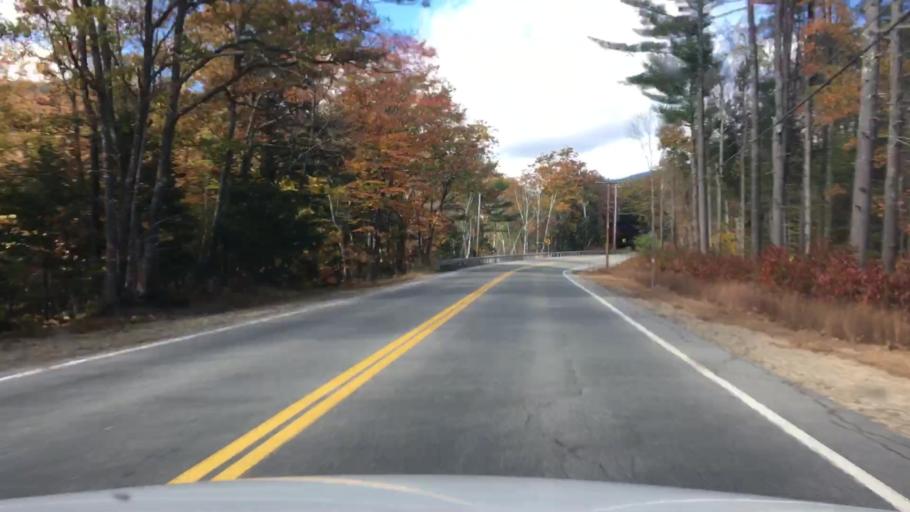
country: US
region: New Hampshire
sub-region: Carroll County
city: North Conway
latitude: 44.1648
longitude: -71.2192
